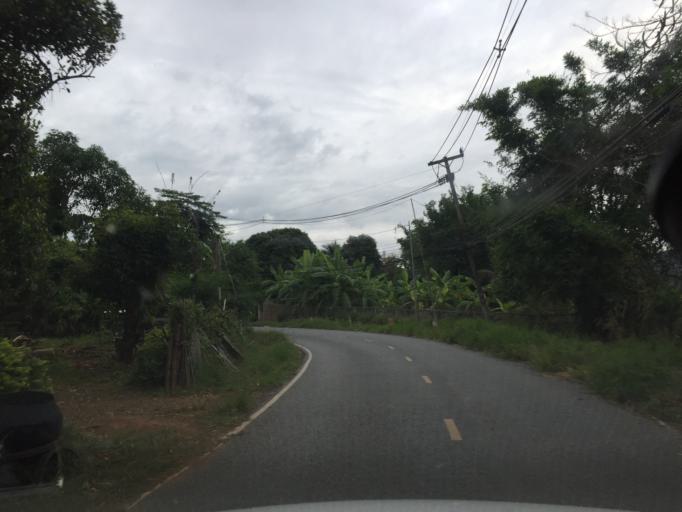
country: TH
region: Chiang Mai
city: Mae On
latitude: 18.8320
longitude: 99.1694
